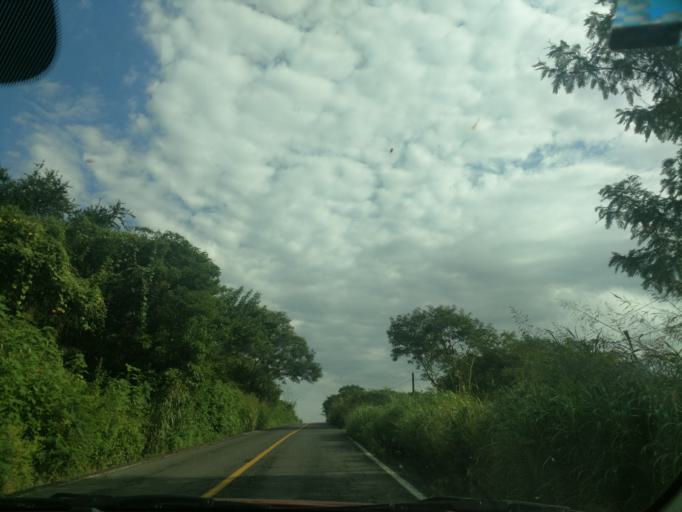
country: MX
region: Jalisco
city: Ameca
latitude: 20.5240
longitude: -104.1269
